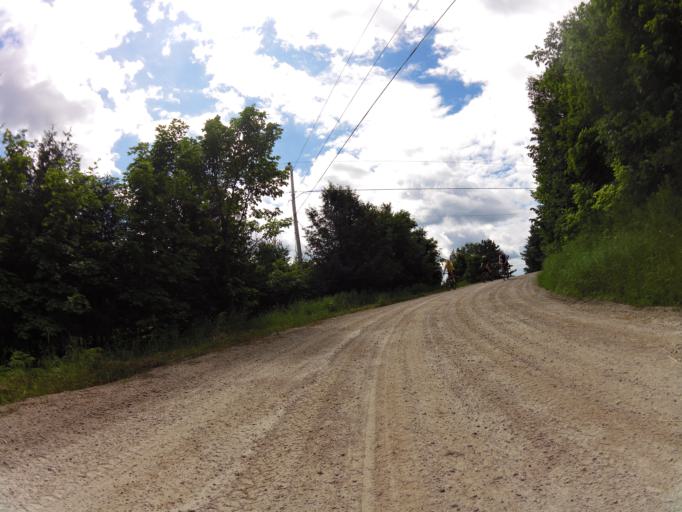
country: CA
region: Ontario
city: Perth
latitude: 45.0283
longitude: -76.5184
